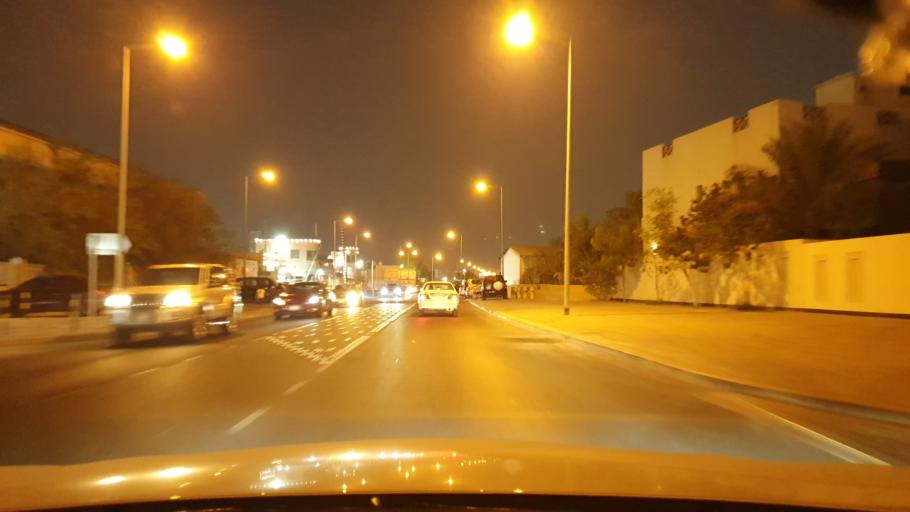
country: BH
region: Muharraq
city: Al Muharraq
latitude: 26.2718
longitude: 50.6144
